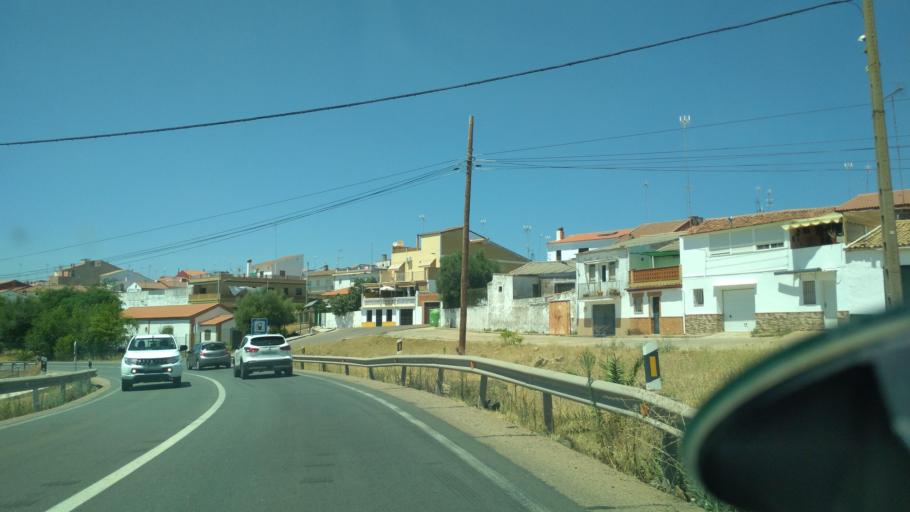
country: ES
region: Andalusia
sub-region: Provincia de Huelva
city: Zalamea la Real
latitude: 37.6915
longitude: -6.6299
